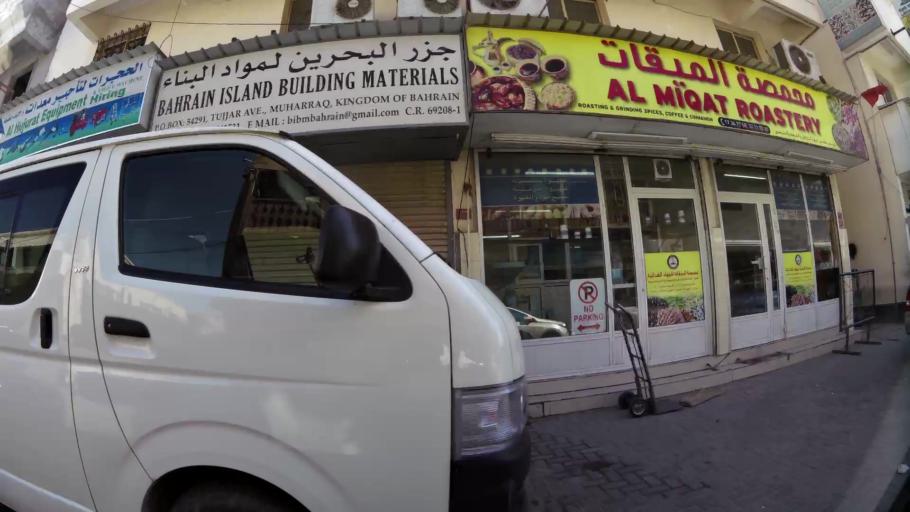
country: BH
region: Muharraq
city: Al Muharraq
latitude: 26.2490
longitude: 50.6103
